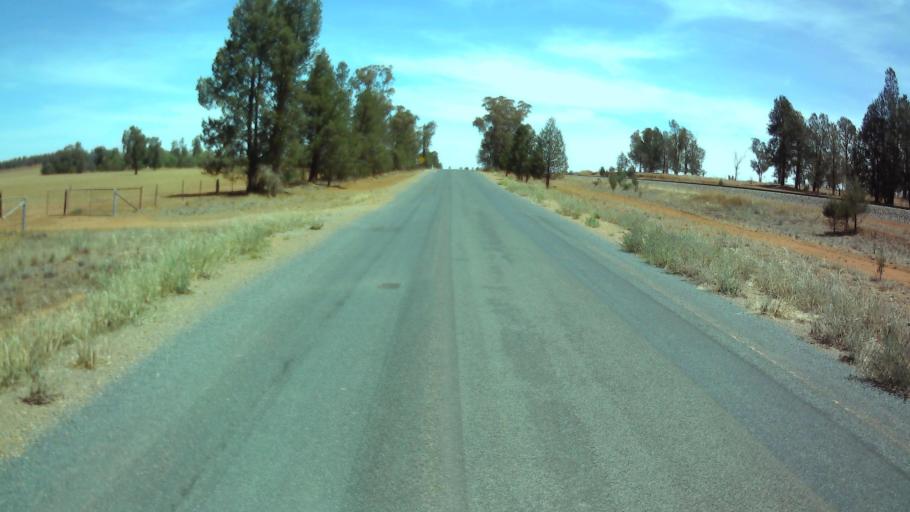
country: AU
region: New South Wales
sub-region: Weddin
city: Grenfell
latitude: -33.7705
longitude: 147.7571
